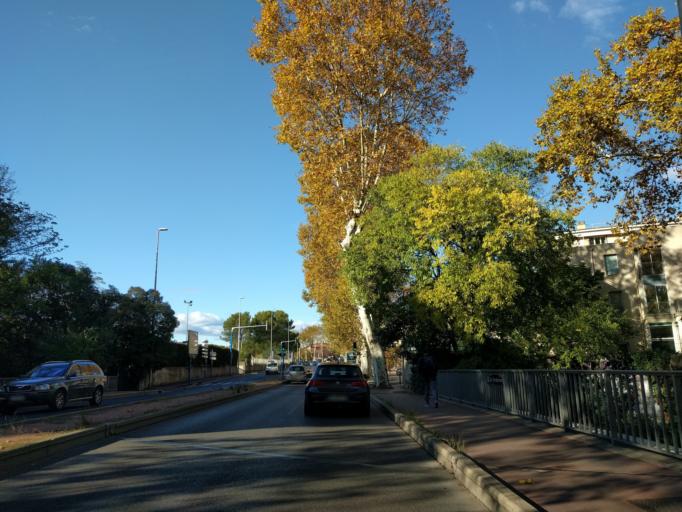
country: FR
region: Languedoc-Roussillon
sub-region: Departement de l'Herault
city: Montpellier
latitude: 43.6210
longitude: 3.8648
